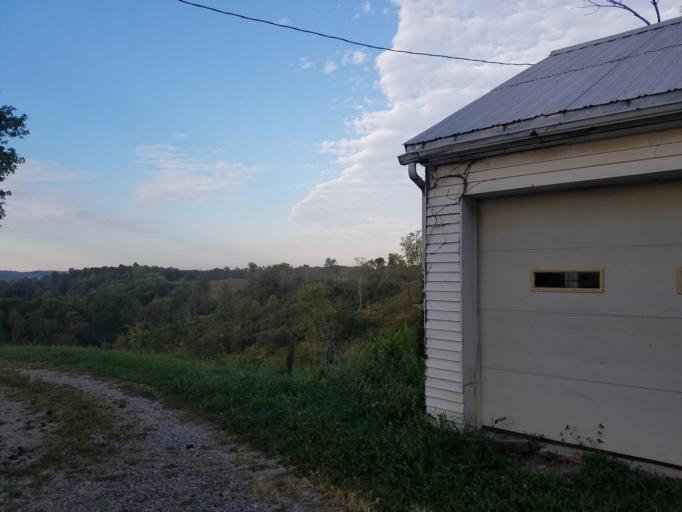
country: US
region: Ohio
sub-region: Belmont County
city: Barnesville
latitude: 40.0917
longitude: -81.3278
